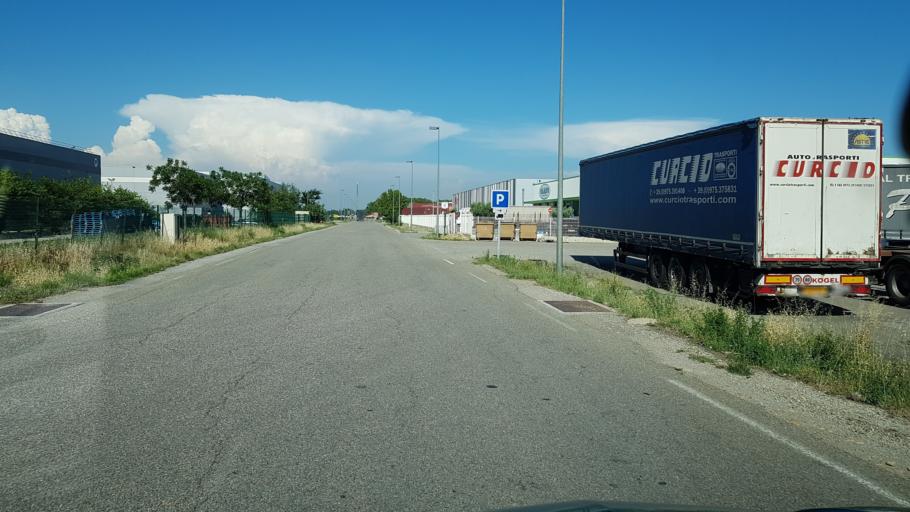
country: FR
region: Provence-Alpes-Cote d'Azur
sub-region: Departement des Bouches-du-Rhone
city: Saint-Martin-de-Crau
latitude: 43.6245
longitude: 4.7947
